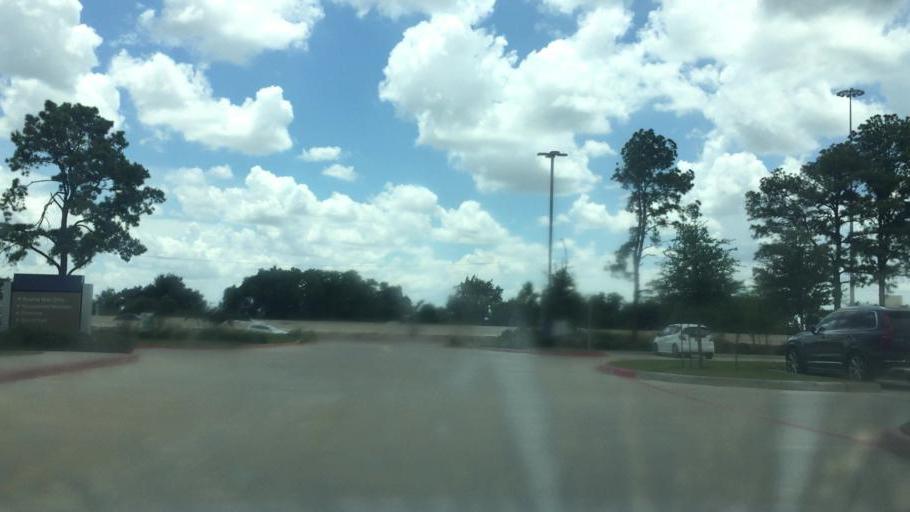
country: US
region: Texas
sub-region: Harris County
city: Cypress
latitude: 29.9864
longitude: -95.7323
